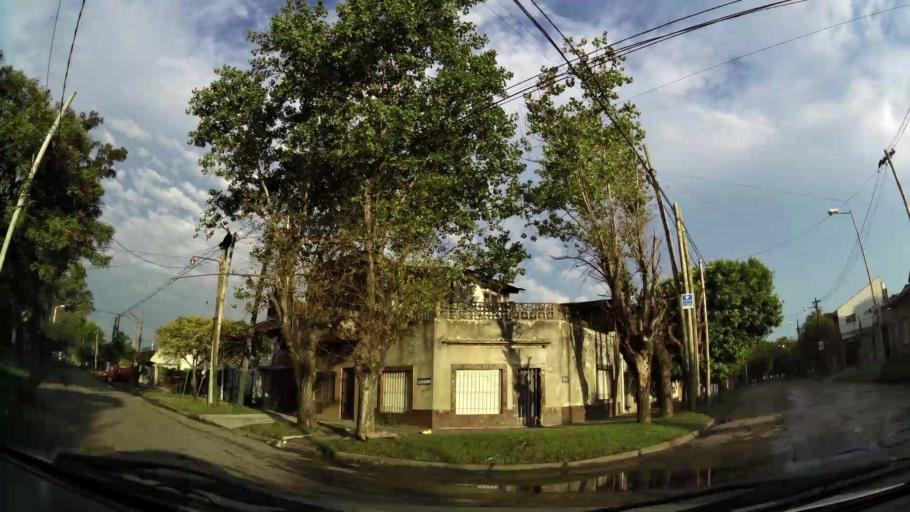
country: AR
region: Buenos Aires
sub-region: Partido de Almirante Brown
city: Adrogue
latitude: -34.7613
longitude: -58.3585
